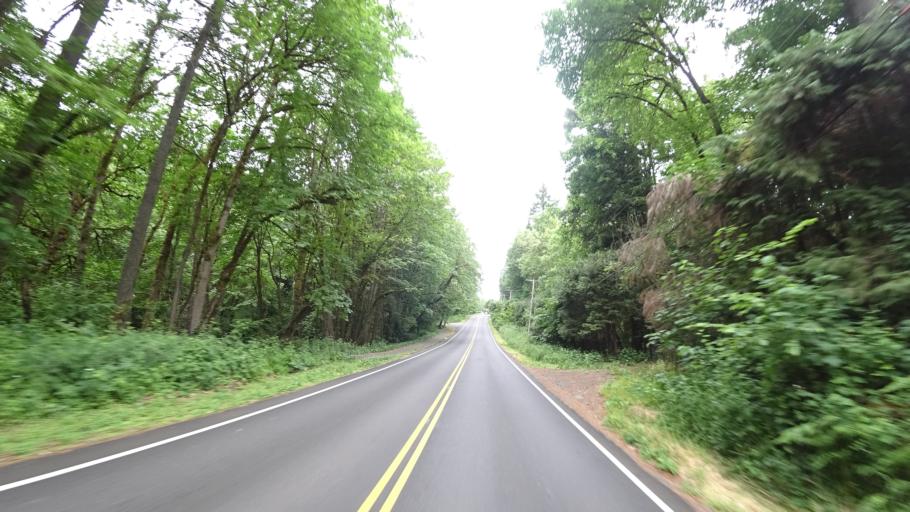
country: US
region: Oregon
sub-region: Clackamas County
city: Lake Oswego
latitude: 45.4313
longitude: -122.6656
